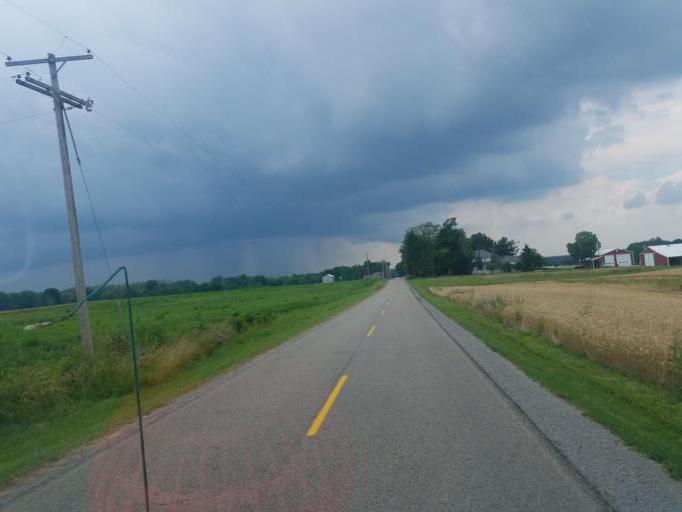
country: US
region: Ohio
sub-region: Mahoning County
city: Sebring
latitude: 40.9740
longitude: -80.9368
